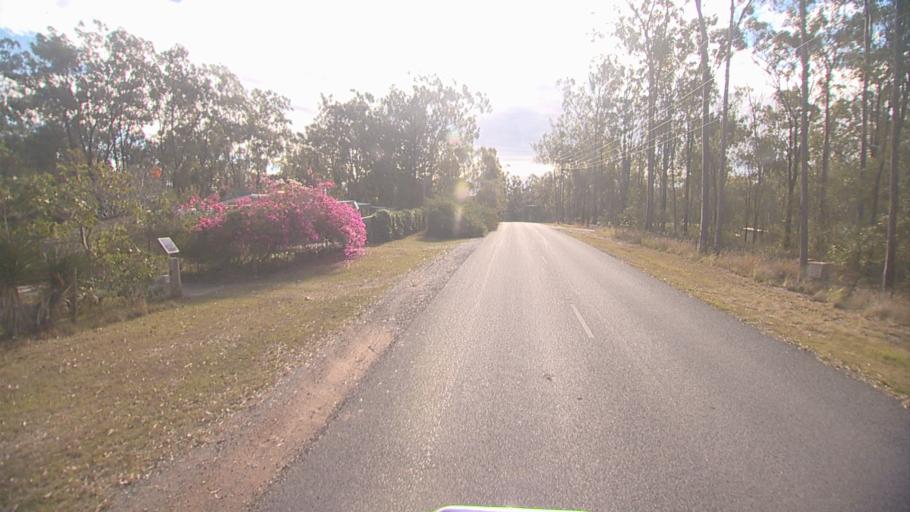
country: AU
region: Queensland
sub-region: Logan
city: Cedar Vale
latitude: -27.8430
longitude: 153.0564
